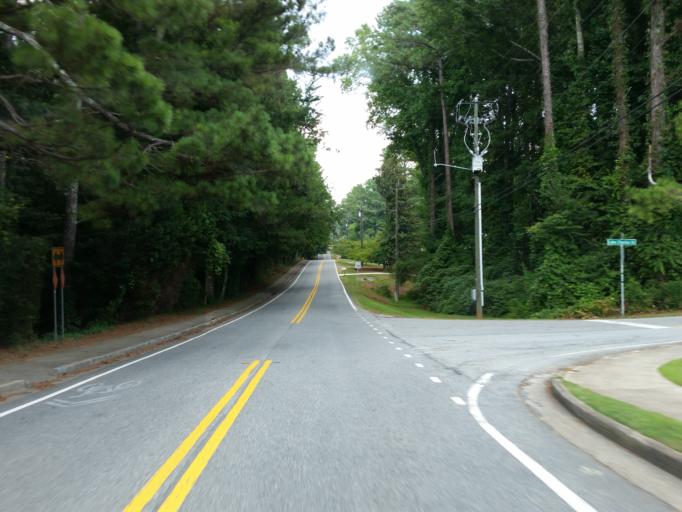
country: US
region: Georgia
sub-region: Fulton County
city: Roswell
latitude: 34.0469
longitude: -84.3829
